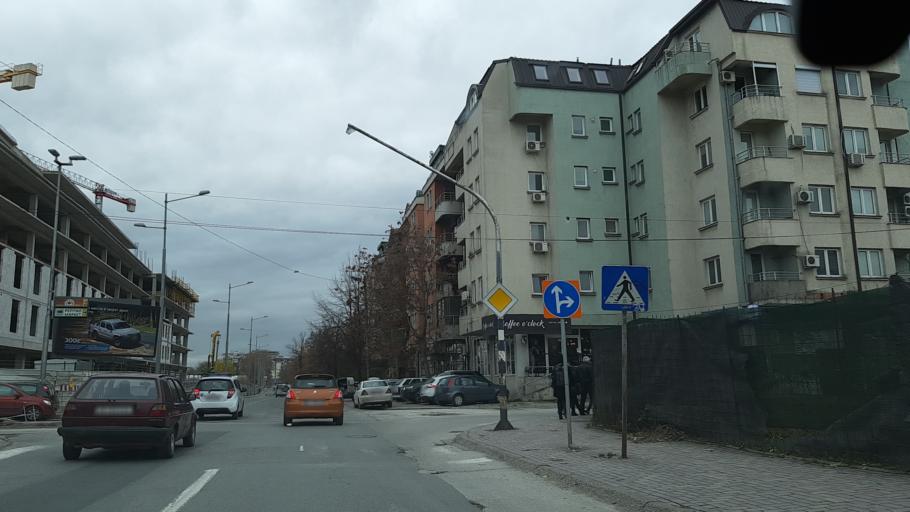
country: MK
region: Karpos
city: Skopje
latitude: 41.9911
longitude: 21.4256
